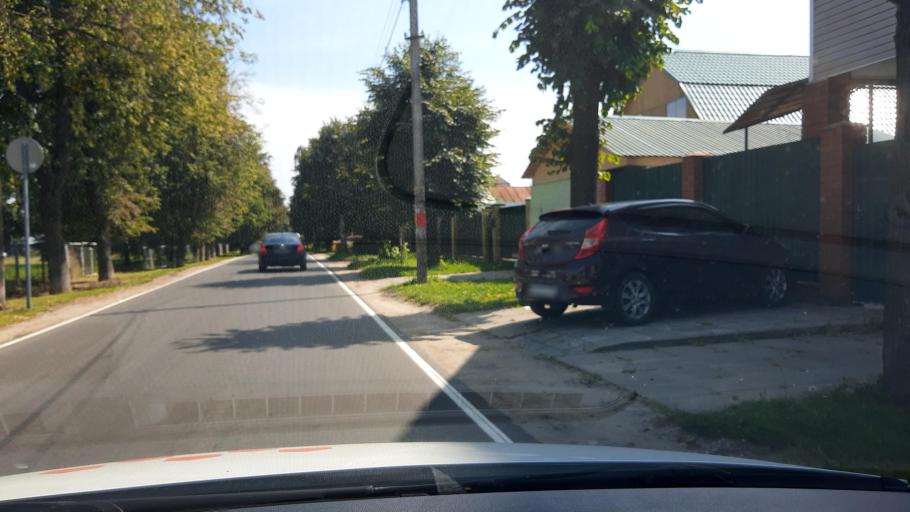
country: RU
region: Moskovskaya
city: Bronnitsy
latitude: 55.4216
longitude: 38.2658
